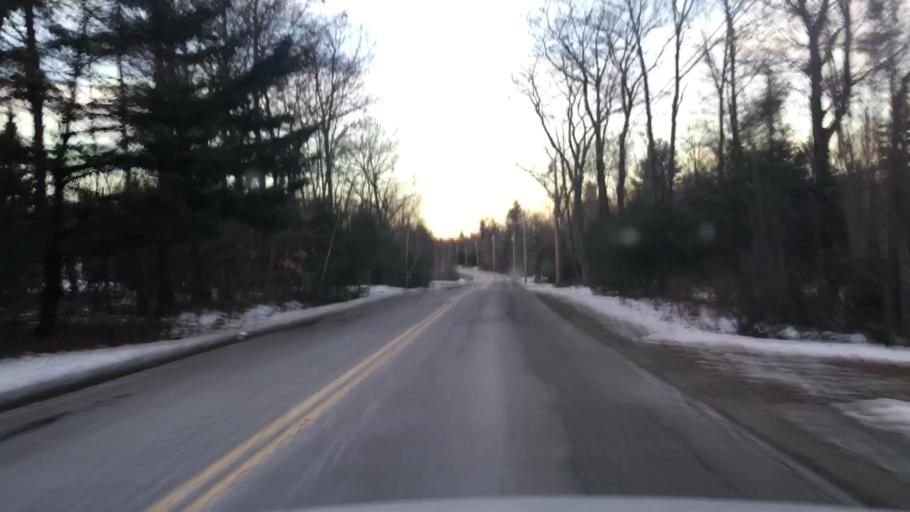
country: US
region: Maine
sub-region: York County
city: Lebanon
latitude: 43.3504
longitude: -70.8670
